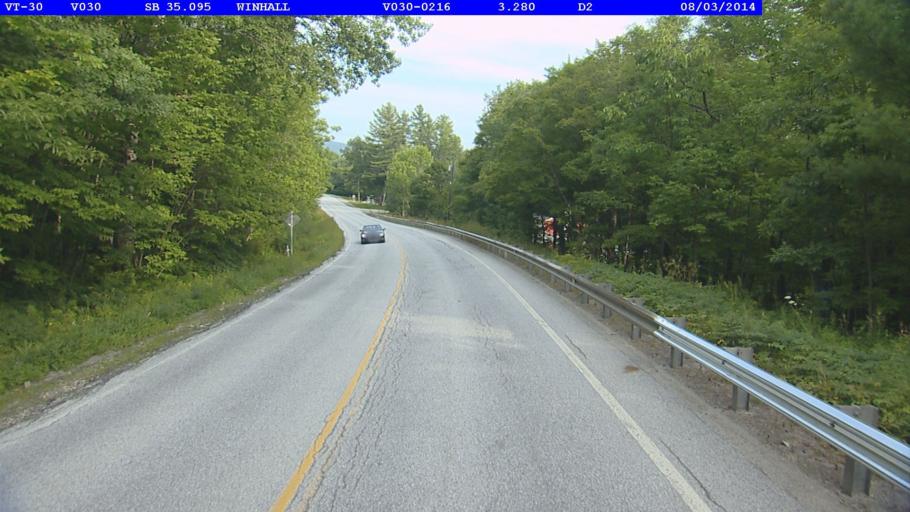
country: US
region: Vermont
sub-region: Bennington County
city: Manchester Center
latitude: 43.1586
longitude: -72.9249
